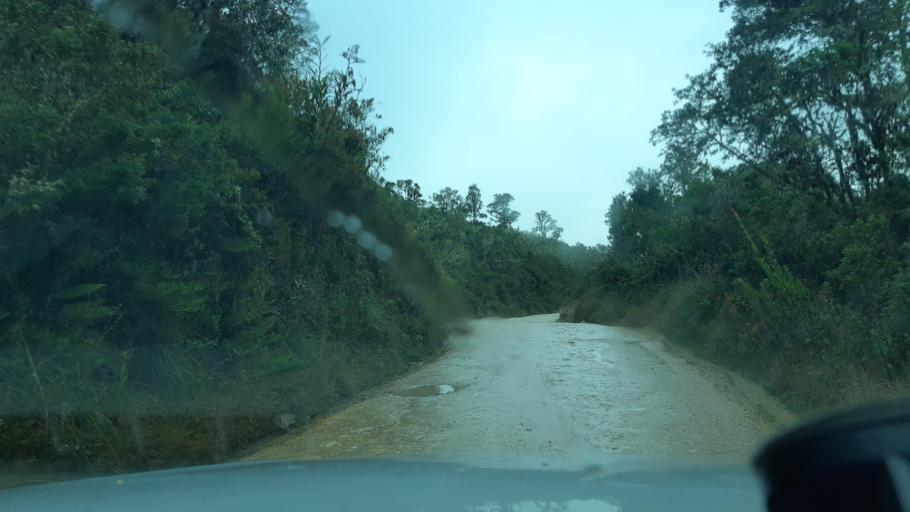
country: CO
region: Cundinamarca
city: Villapinzon
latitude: 5.2168
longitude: -73.5329
